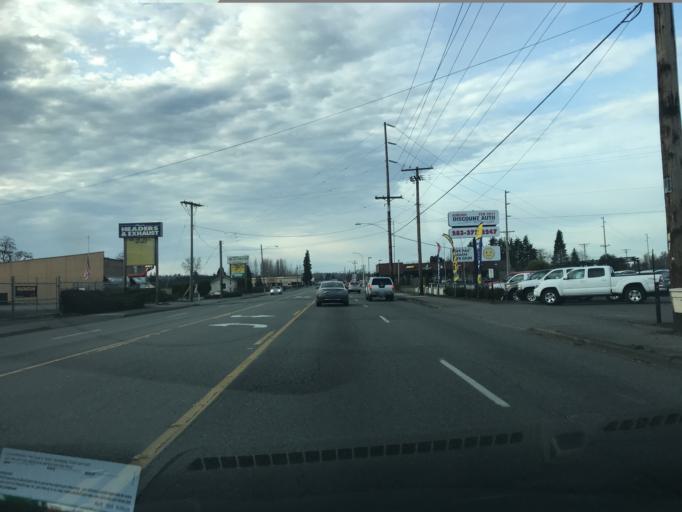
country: US
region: Washington
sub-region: King County
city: Kent
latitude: 47.3488
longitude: -122.2244
